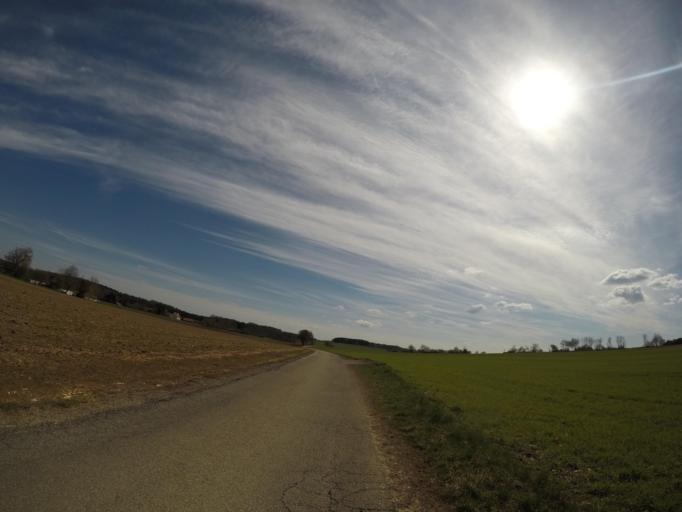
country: DE
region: Baden-Wuerttemberg
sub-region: Tuebingen Region
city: Mehrstetten
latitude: 48.3454
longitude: 9.5650
